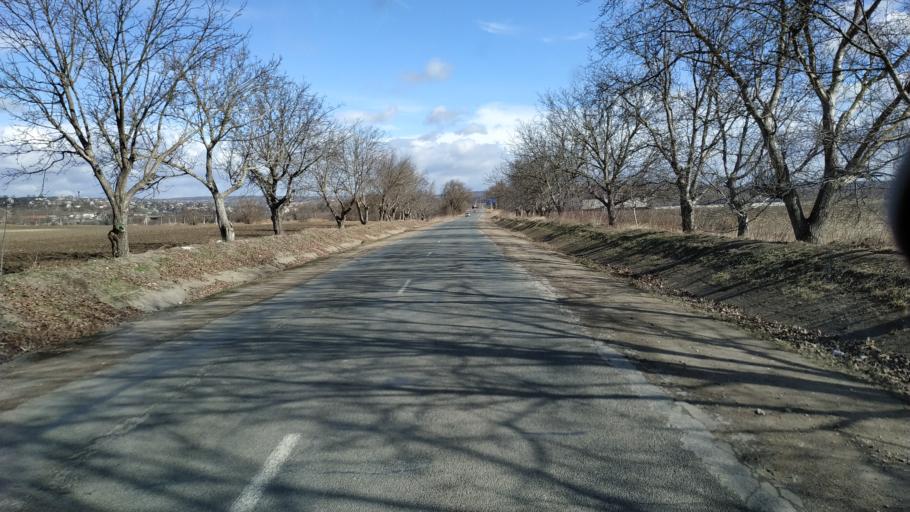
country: MD
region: Stinga Nistrului
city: Bucovat
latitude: 47.1772
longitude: 28.4615
